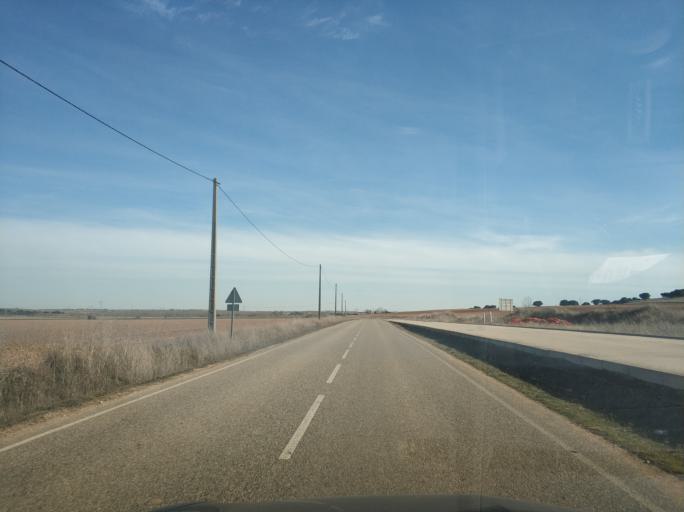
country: ES
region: Castille and Leon
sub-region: Provincia de Salamanca
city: Florida de Liebana
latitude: 41.0252
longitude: -5.7581
